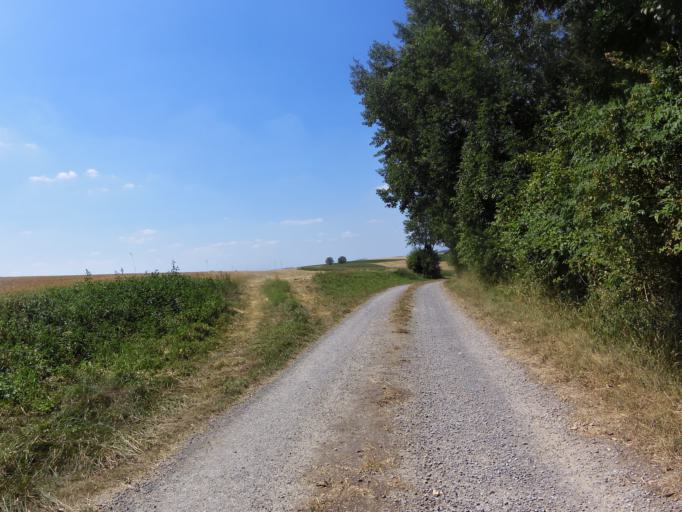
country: DE
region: Bavaria
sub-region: Regierungsbezirk Unterfranken
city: Rimpar
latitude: 49.8280
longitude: 9.9461
